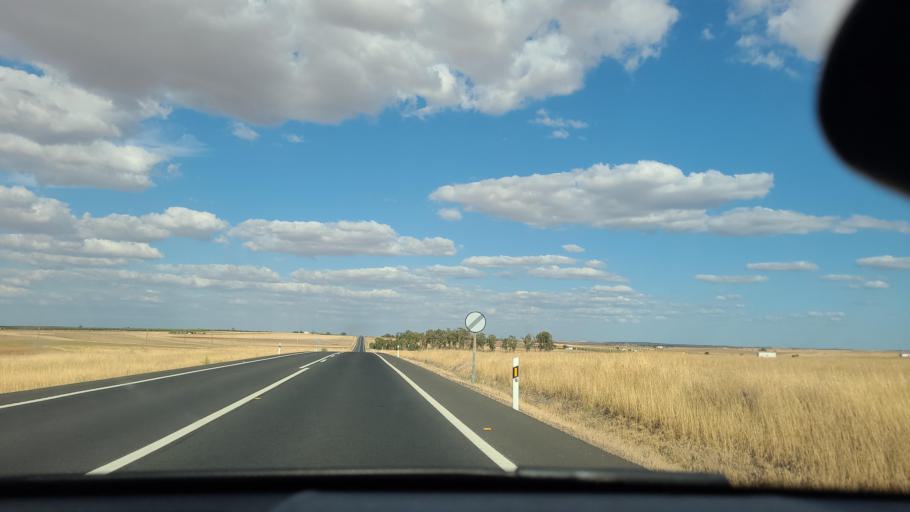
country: ES
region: Extremadura
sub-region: Provincia de Badajoz
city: Ahillones
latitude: 38.2556
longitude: -5.9018
